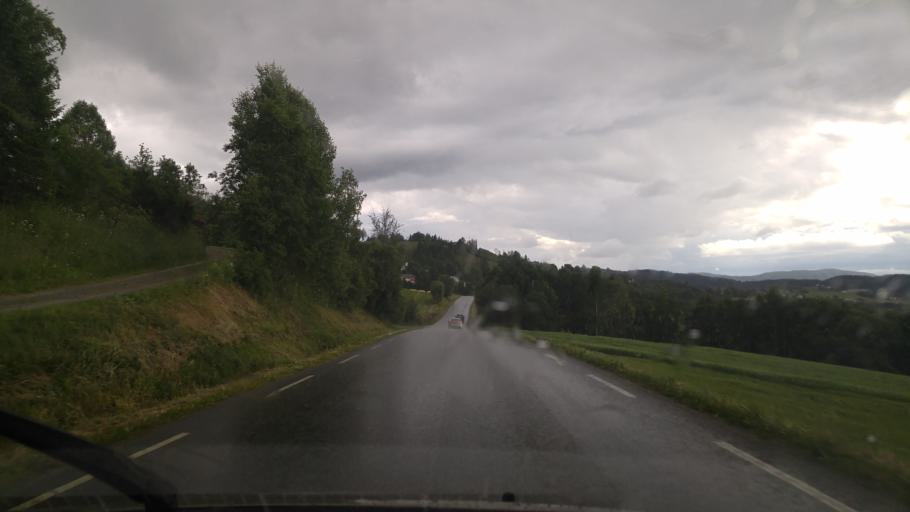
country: NO
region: Nord-Trondelag
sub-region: Levanger
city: Skogn
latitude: 63.6779
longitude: 11.2435
